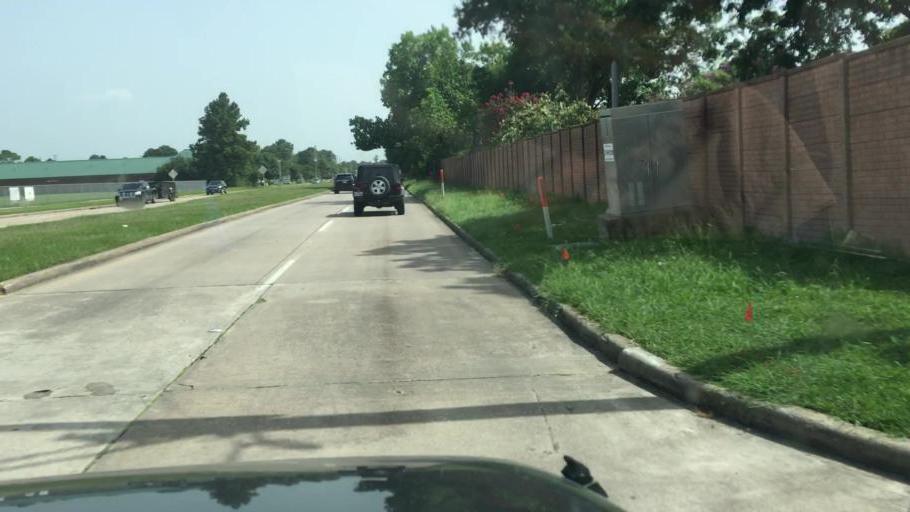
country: US
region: Texas
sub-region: Harris County
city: Atascocita
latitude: 29.9924
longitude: -95.1618
